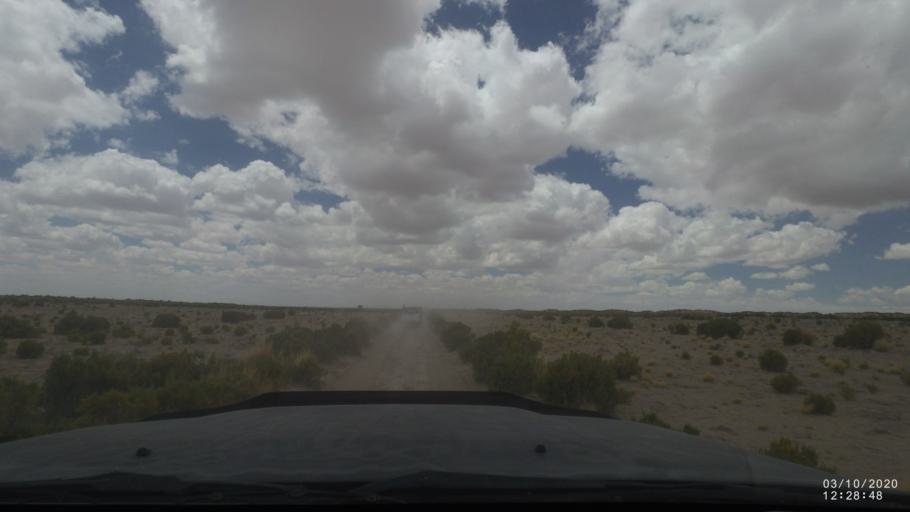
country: BO
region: Oruro
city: Poopo
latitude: -18.6902
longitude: -67.5502
